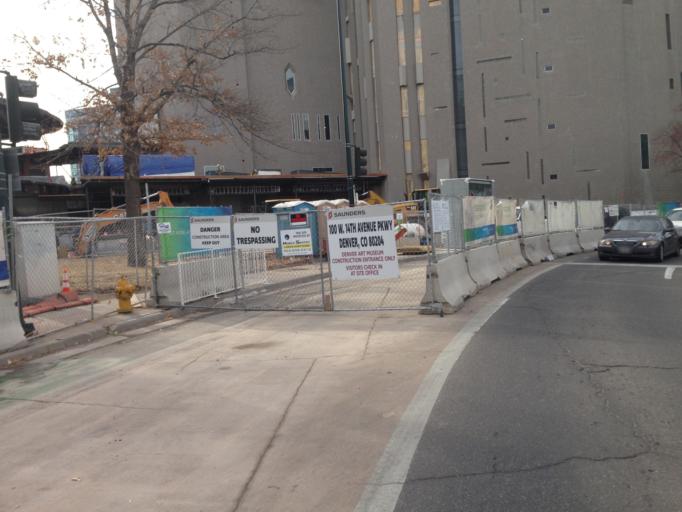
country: US
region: Colorado
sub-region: Denver County
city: Denver
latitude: 39.7378
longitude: -104.9889
